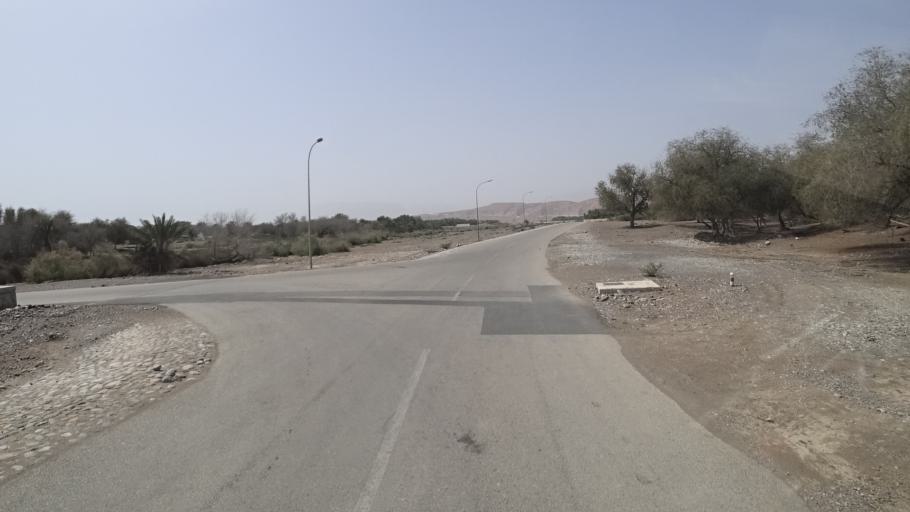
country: OM
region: Muhafazat Masqat
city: Muscat
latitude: 23.2129
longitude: 58.9738
